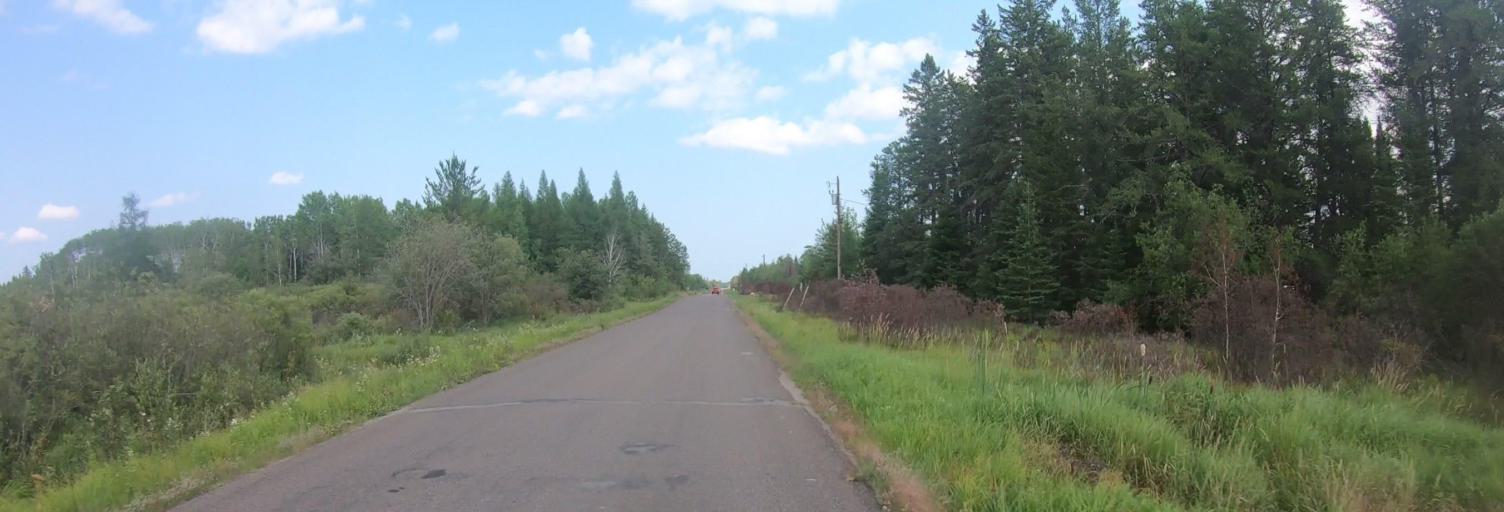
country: US
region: Minnesota
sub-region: Saint Louis County
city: Mountain Iron
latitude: 47.8918
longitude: -92.6894
